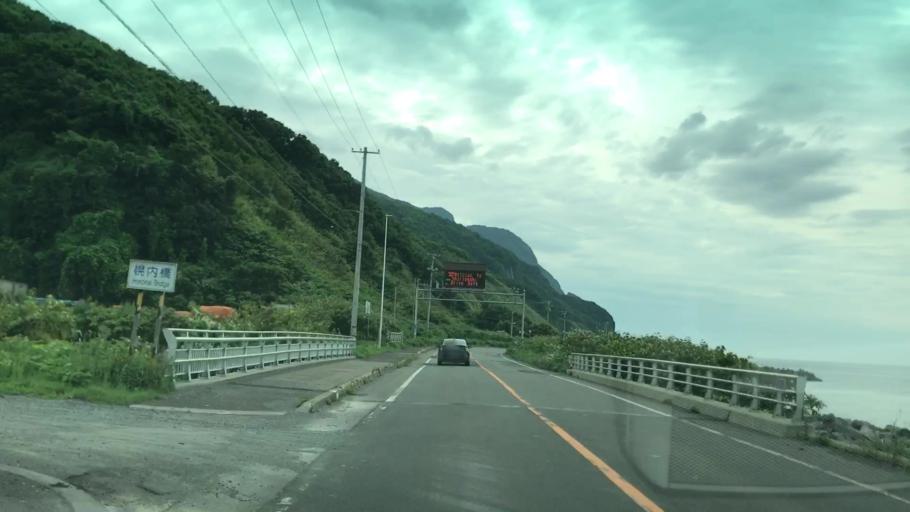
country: JP
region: Hokkaido
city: Iwanai
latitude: 42.9633
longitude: 140.4663
